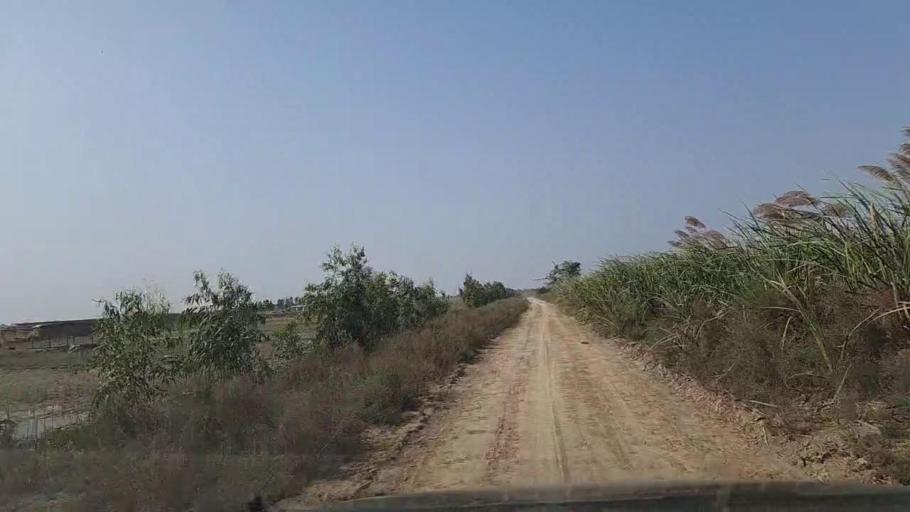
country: PK
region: Sindh
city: Gharo
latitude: 24.7295
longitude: 67.7224
